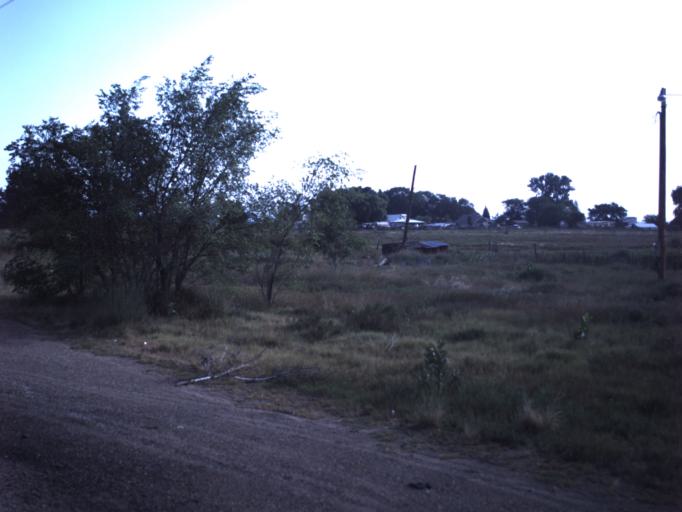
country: US
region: Utah
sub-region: Duchesne County
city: Duchesne
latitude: 40.3451
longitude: -110.2752
